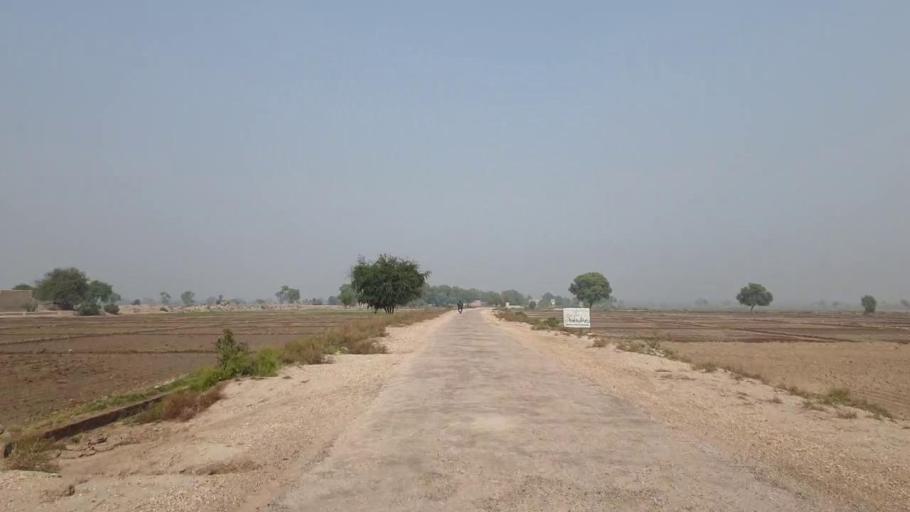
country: PK
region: Sindh
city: Bhan
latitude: 26.5200
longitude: 67.6899
